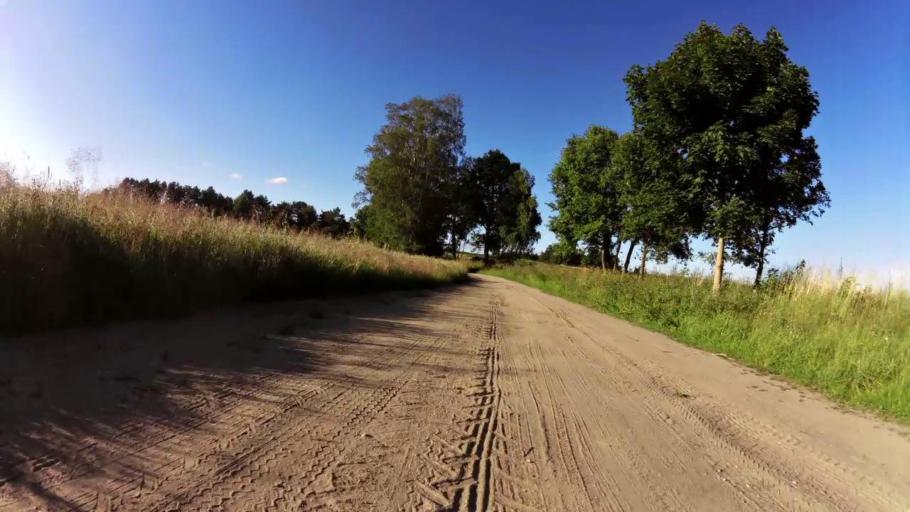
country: PL
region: West Pomeranian Voivodeship
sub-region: Powiat swidwinski
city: Swidwin
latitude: 53.7067
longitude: 15.8285
